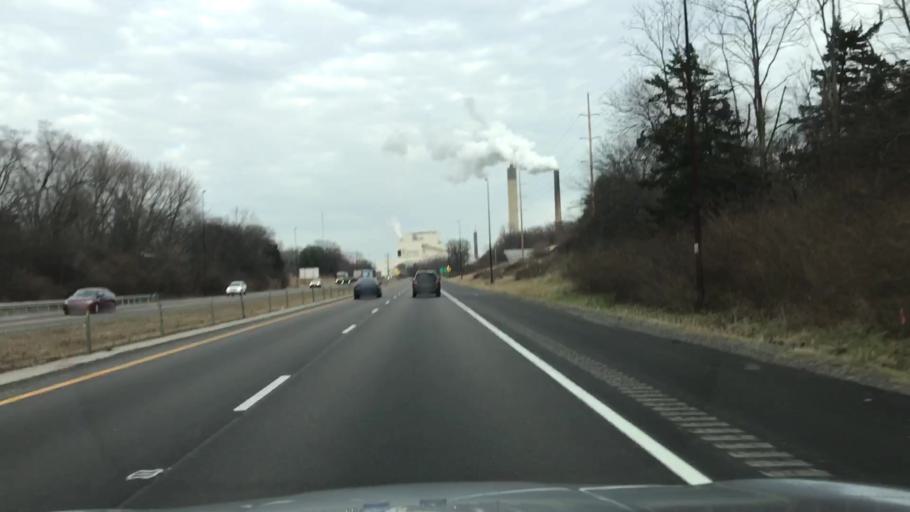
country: US
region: Illinois
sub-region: Sangamon County
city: Southern View
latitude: 39.7499
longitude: -89.6160
